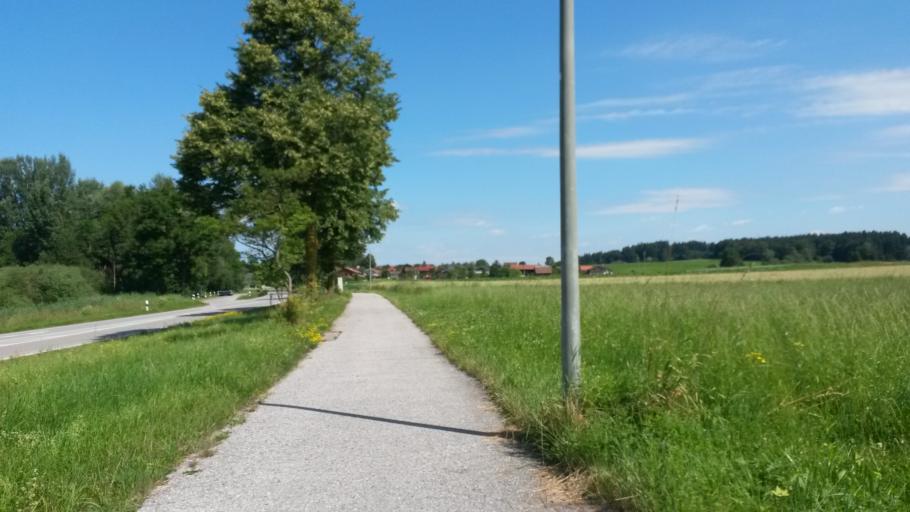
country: DE
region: Bavaria
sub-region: Upper Bavaria
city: Grabenstatt
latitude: 47.8516
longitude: 12.5410
